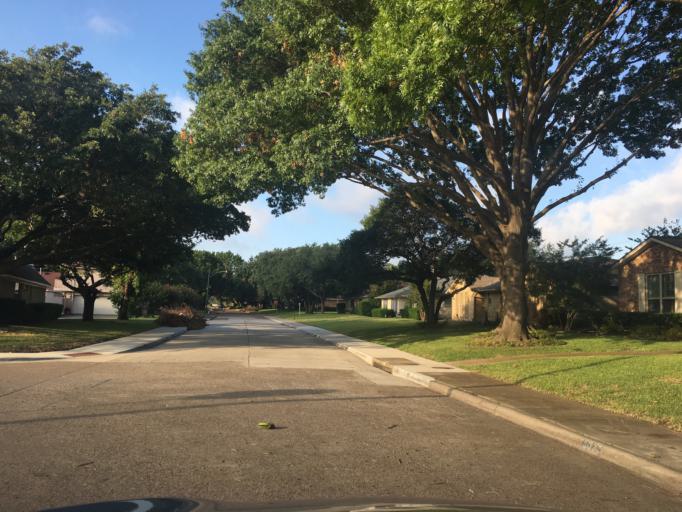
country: US
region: Texas
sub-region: Dallas County
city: Highland Park
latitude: 32.8496
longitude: -96.7603
